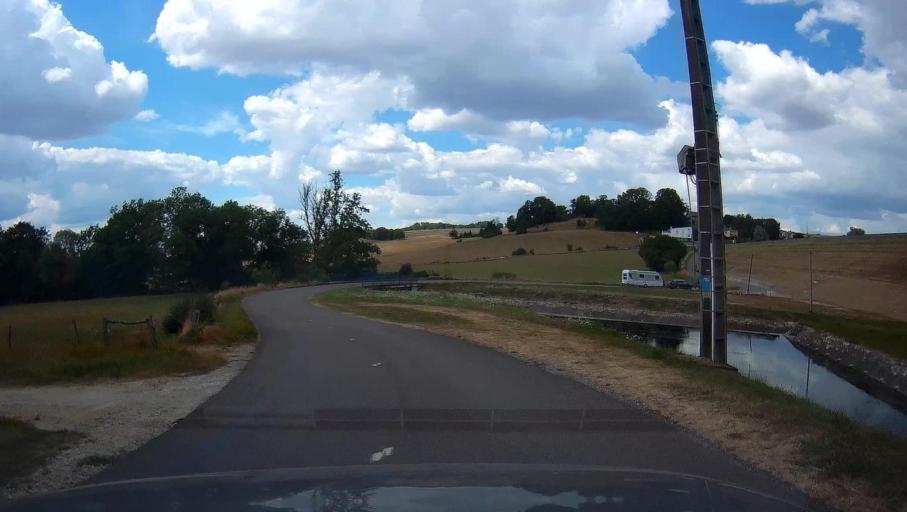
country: FR
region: Champagne-Ardenne
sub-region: Departement de la Haute-Marne
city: Langres
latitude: 47.8653
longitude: 5.3733
